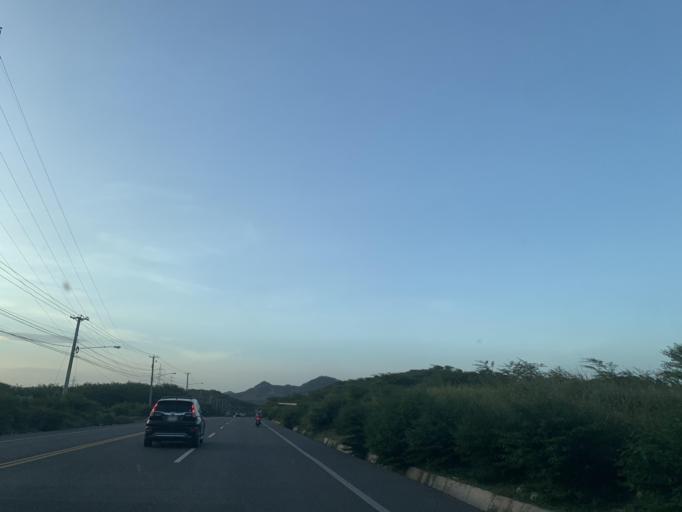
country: DO
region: Puerto Plata
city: Imbert
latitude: 19.7463
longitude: -70.8401
